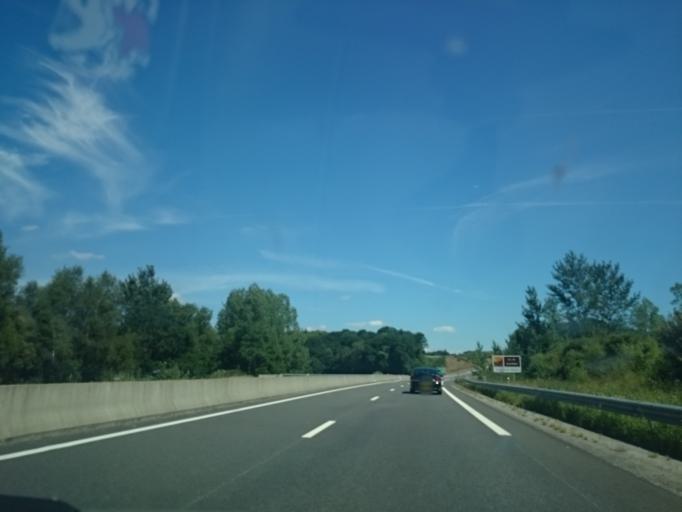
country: FR
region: Brittany
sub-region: Departement des Cotes-d'Armor
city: Gouarec
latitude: 48.2276
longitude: -3.1135
